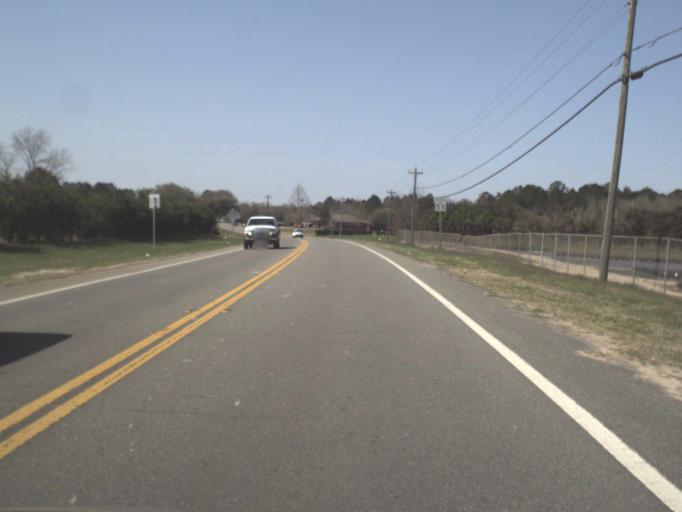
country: US
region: Florida
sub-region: Gadsden County
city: Havana
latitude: 30.6199
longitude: -84.4326
